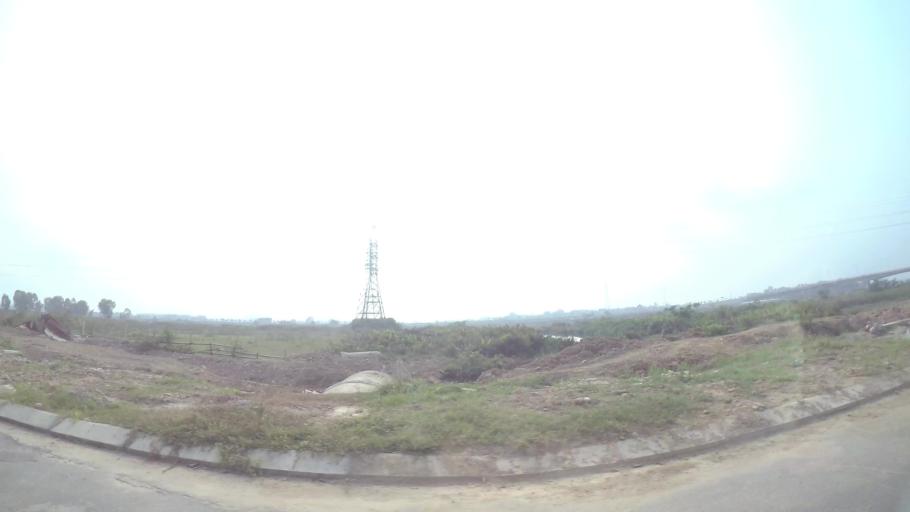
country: VN
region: Da Nang
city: Ngu Hanh Son
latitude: 16.0050
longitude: 108.2292
